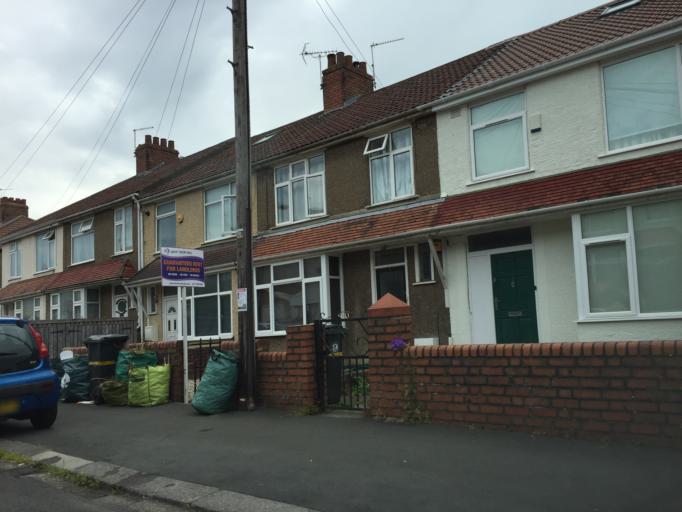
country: GB
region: England
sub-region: Bristol
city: Bristol
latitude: 51.4927
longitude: -2.5785
